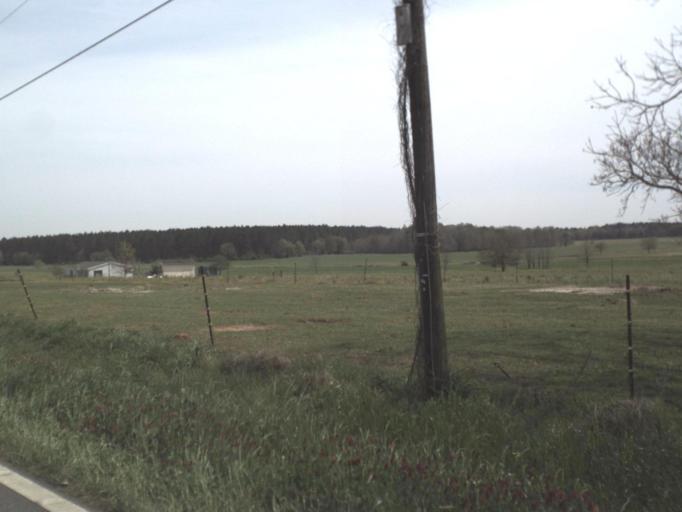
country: US
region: Florida
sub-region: Jackson County
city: Graceville
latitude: 30.9530
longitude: -85.4244
